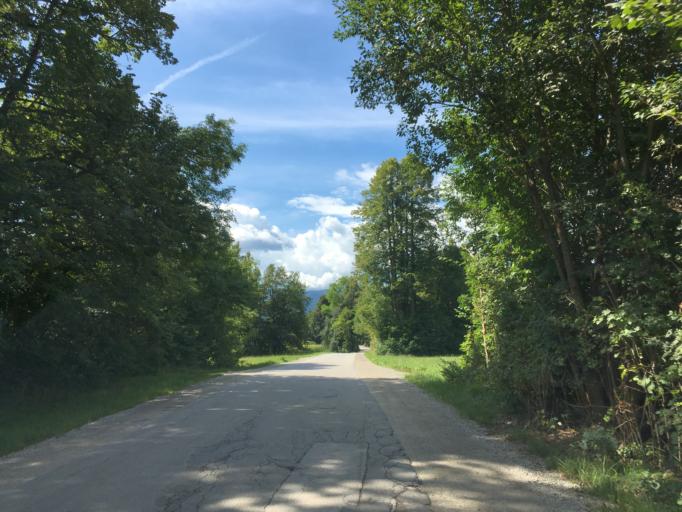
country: SI
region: Radovljica
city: Lesce
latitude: 46.3744
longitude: 14.1690
